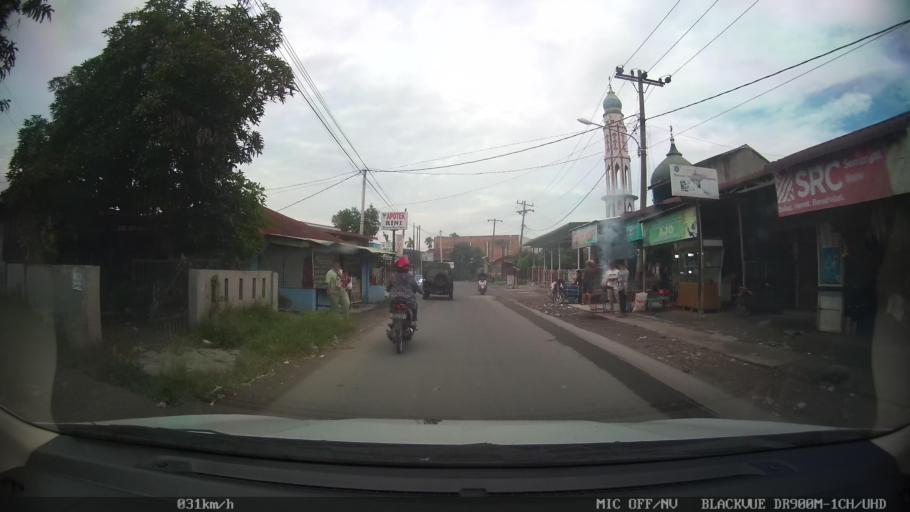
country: ID
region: North Sumatra
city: Sunggal
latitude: 3.6204
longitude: 98.5976
